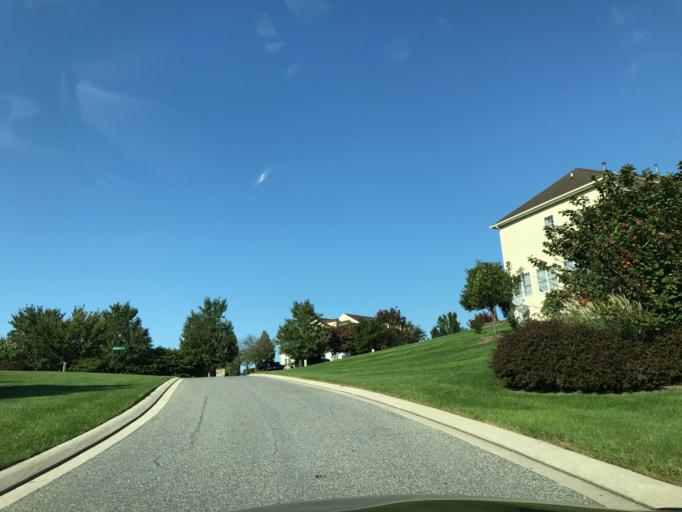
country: US
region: Maryland
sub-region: Baltimore County
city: Hunt Valley
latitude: 39.5271
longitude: -76.6165
